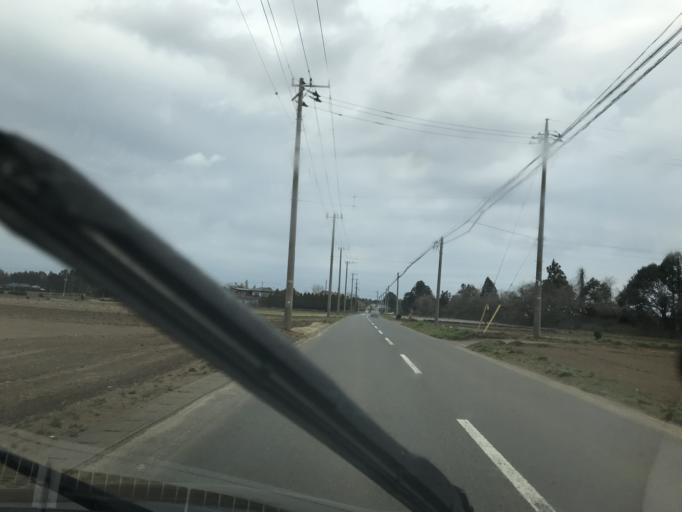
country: JP
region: Chiba
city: Sawara
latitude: 35.8377
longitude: 140.4953
